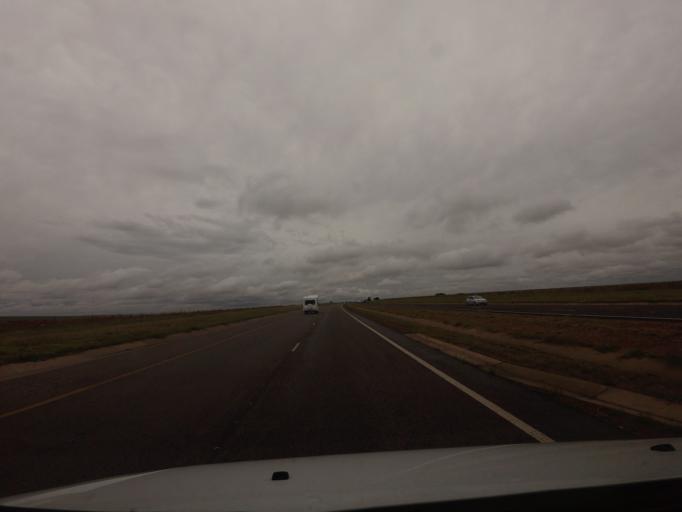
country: ZA
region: Mpumalanga
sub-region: Nkangala District Municipality
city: Middelburg
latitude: -25.8162
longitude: 29.6027
